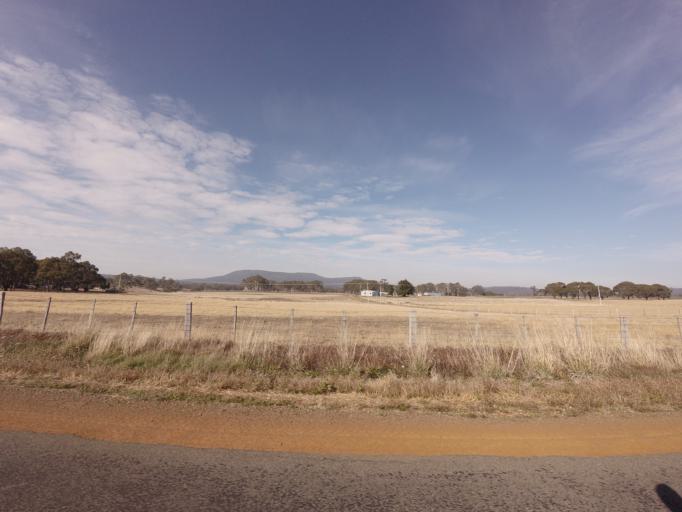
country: AU
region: Tasmania
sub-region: Sorell
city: Sorell
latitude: -42.4477
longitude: 147.4630
